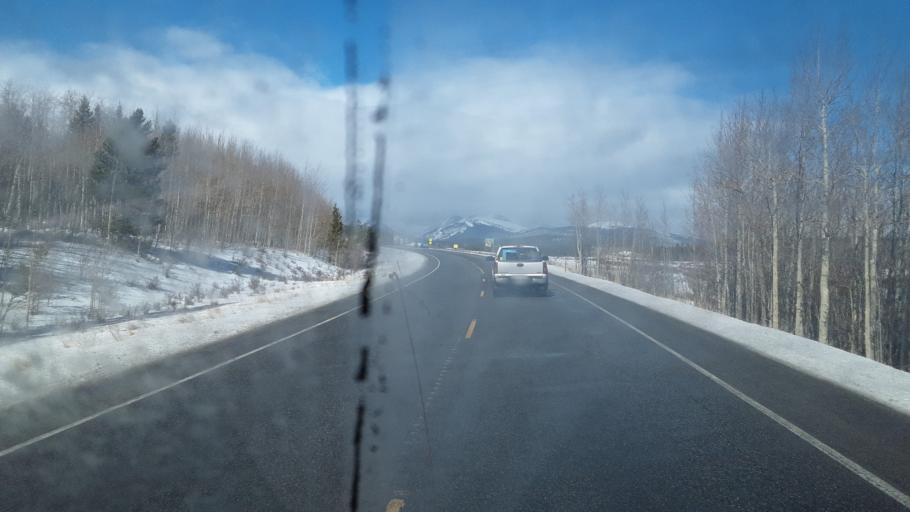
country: US
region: Colorado
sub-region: Summit County
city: Breckenridge
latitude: 39.4099
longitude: -105.7564
